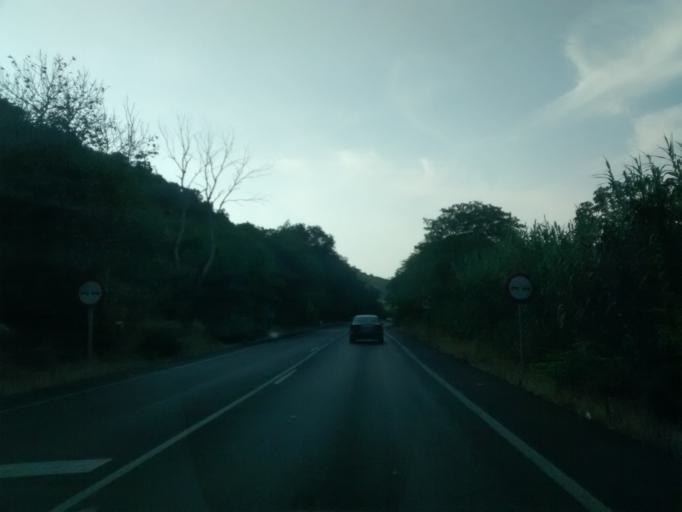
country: ES
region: Andalusia
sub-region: Provincia de Cadiz
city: Vejer de la Frontera
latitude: 36.2552
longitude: -5.9584
